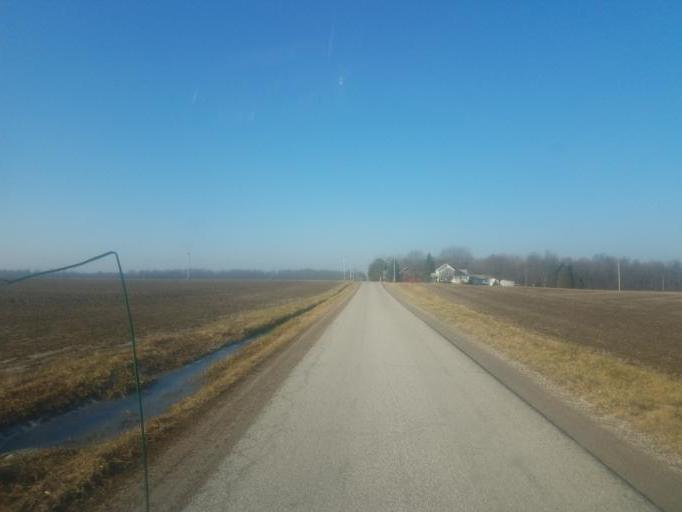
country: US
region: Ohio
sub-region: Crawford County
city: Bucyrus
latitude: 41.0373
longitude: -82.9557
